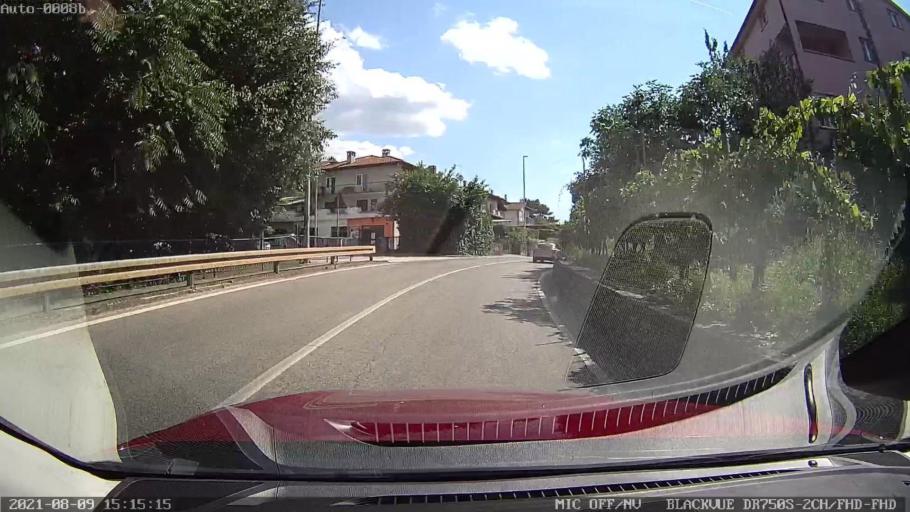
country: HR
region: Istarska
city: Pazin
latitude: 45.2370
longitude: 13.9244
